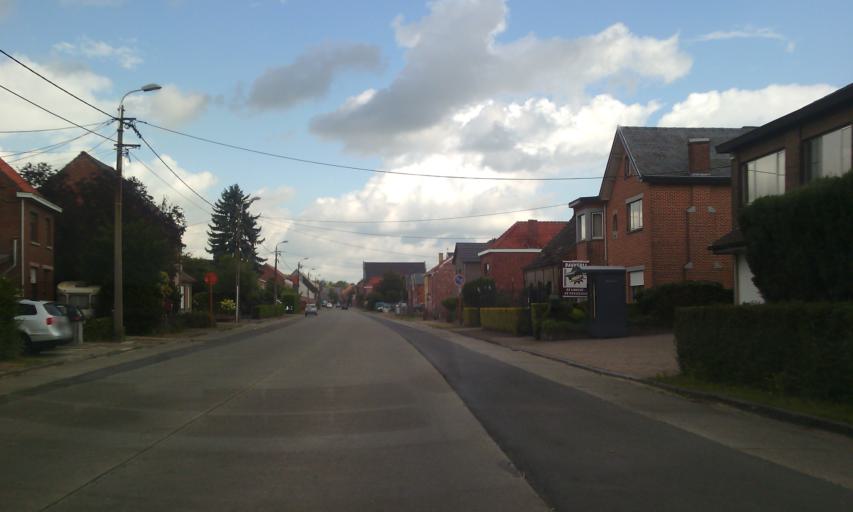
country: BE
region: Flanders
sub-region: Provincie Oost-Vlaanderen
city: Moerbeke
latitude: 51.1422
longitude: 3.9556
